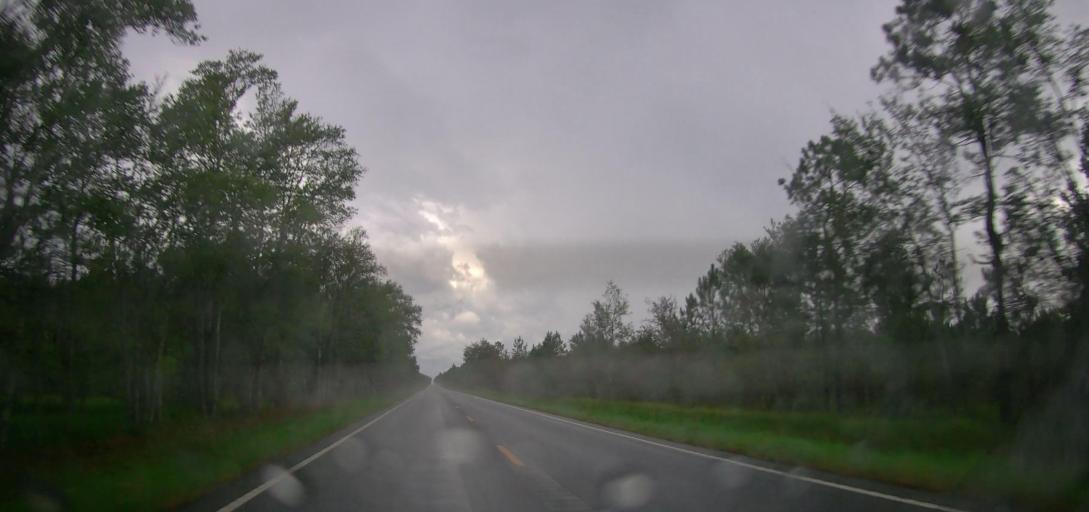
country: US
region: Georgia
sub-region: Brantley County
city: Nahunta
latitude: 31.3428
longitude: -81.8178
